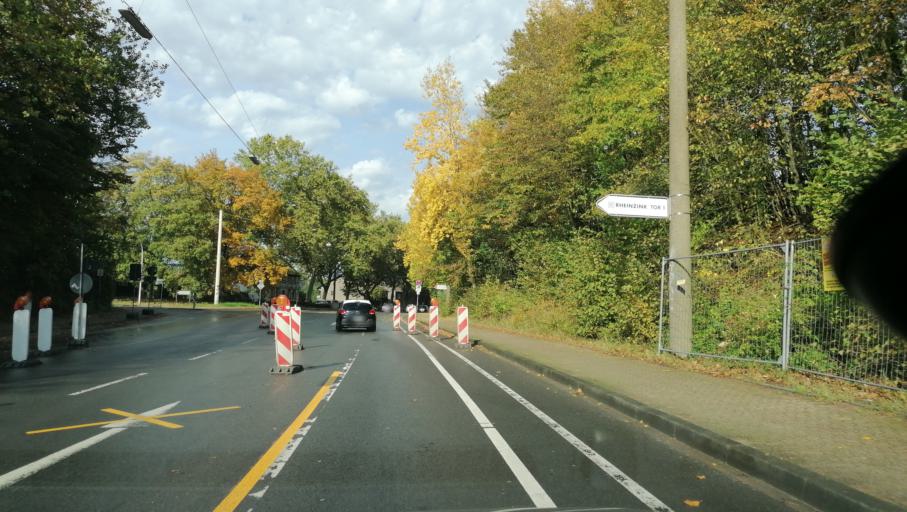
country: DE
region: North Rhine-Westphalia
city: Oer-Erkenschwick
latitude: 51.6253
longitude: 7.3231
